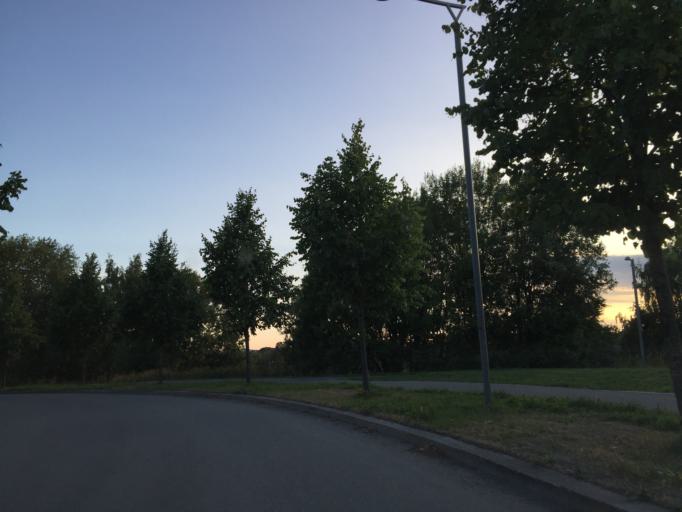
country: NO
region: Akershus
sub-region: Baerum
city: Lysaker
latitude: 59.8979
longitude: 10.6089
